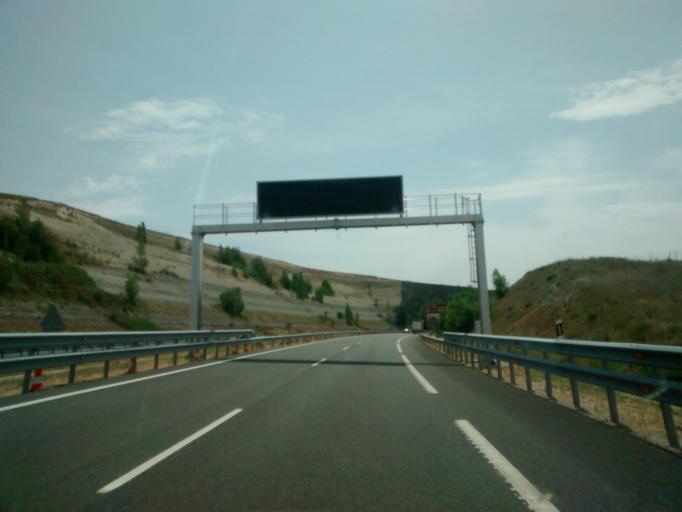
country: ES
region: Castille and Leon
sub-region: Provincia de Burgos
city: Tardajos
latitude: 42.3592
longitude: -3.8041
